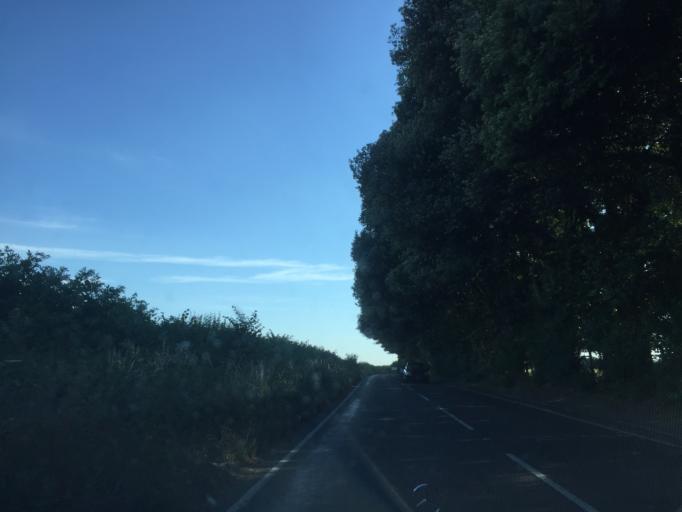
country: GB
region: England
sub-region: Oxfordshire
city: Watlington
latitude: 51.6541
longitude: -0.9950
